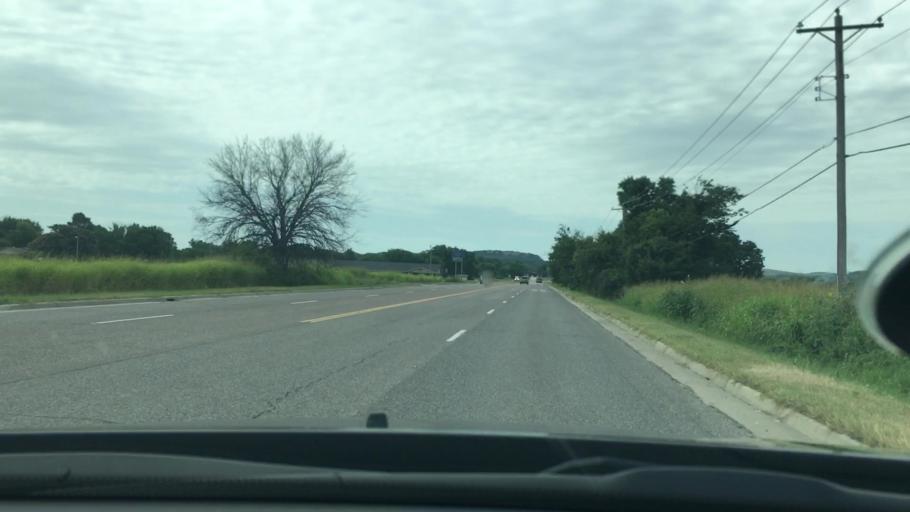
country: US
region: Oklahoma
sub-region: Murray County
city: Davis
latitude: 34.4698
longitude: -97.1313
